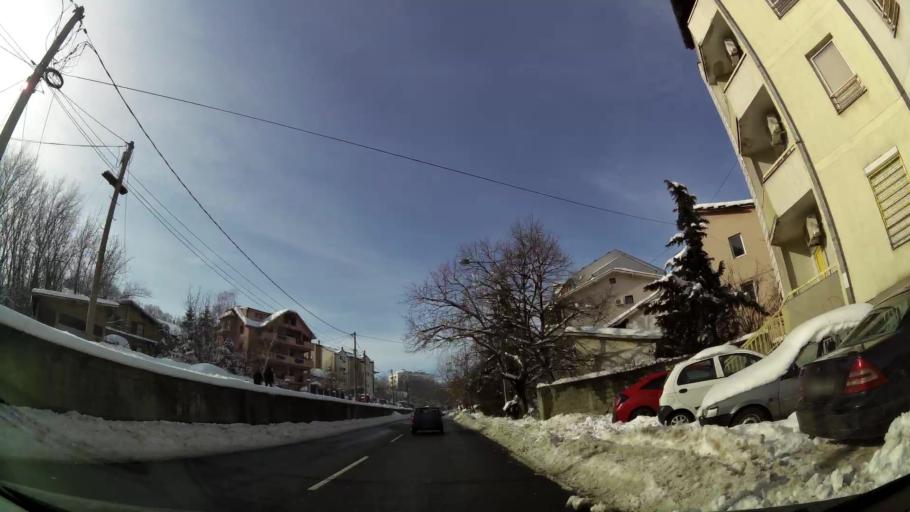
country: RS
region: Central Serbia
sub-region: Belgrade
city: Zvezdara
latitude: 44.7910
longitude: 20.5216
